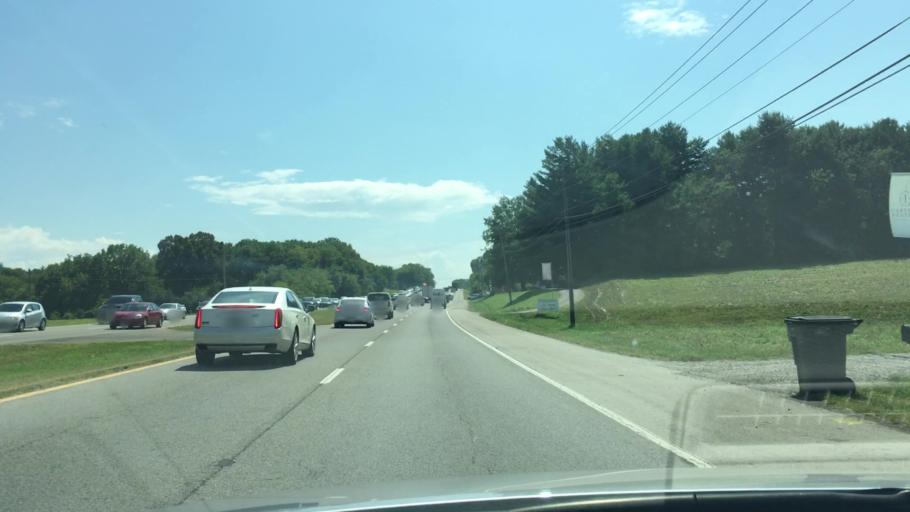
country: US
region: Tennessee
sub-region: Maury County
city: Spring Hill
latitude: 35.7021
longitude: -86.9801
